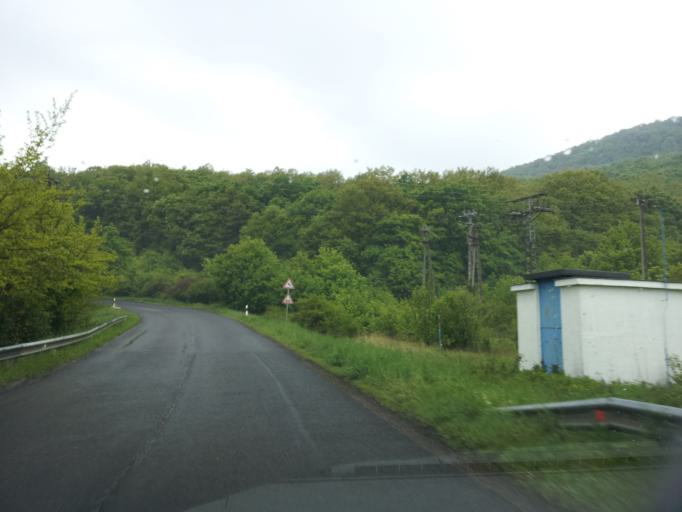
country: HU
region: Baranya
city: Hosszuheteny
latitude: 46.1703
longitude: 18.3413
